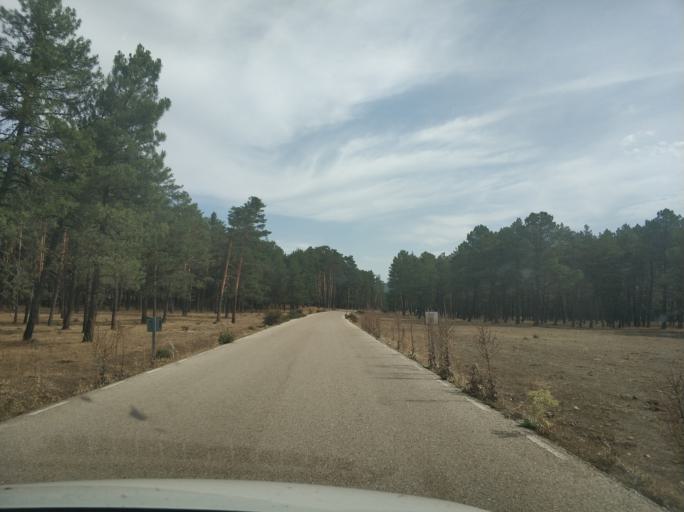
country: ES
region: Castille and Leon
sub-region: Provincia de Soria
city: Navaleno
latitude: 41.8581
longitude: -2.9438
